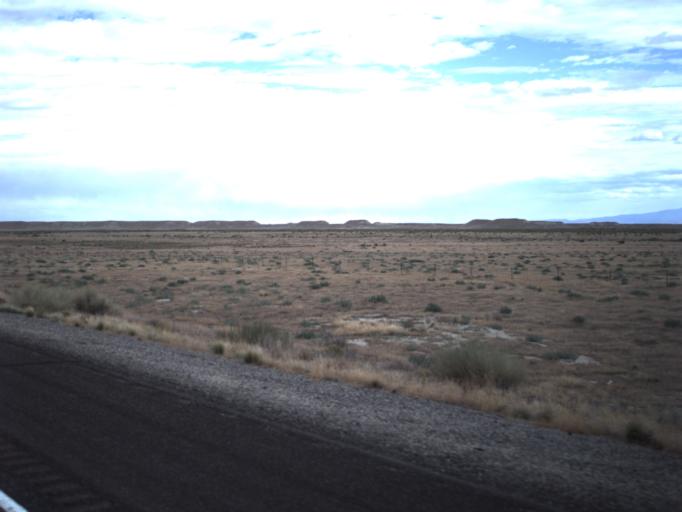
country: US
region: Utah
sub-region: Grand County
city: Moab
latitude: 38.9516
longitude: -109.7681
